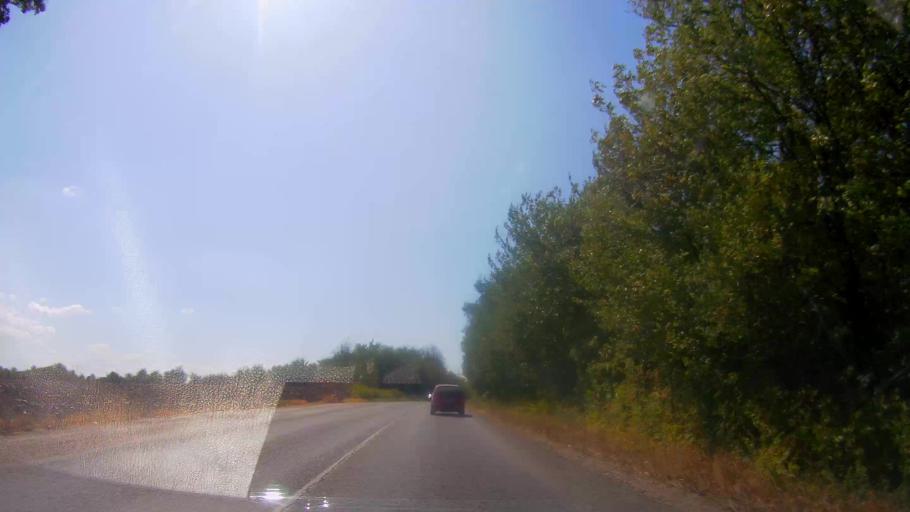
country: BG
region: Veliko Turnovo
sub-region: Obshtina Gorna Oryakhovitsa
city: Purvomaytsi
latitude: 43.2469
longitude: 25.6445
